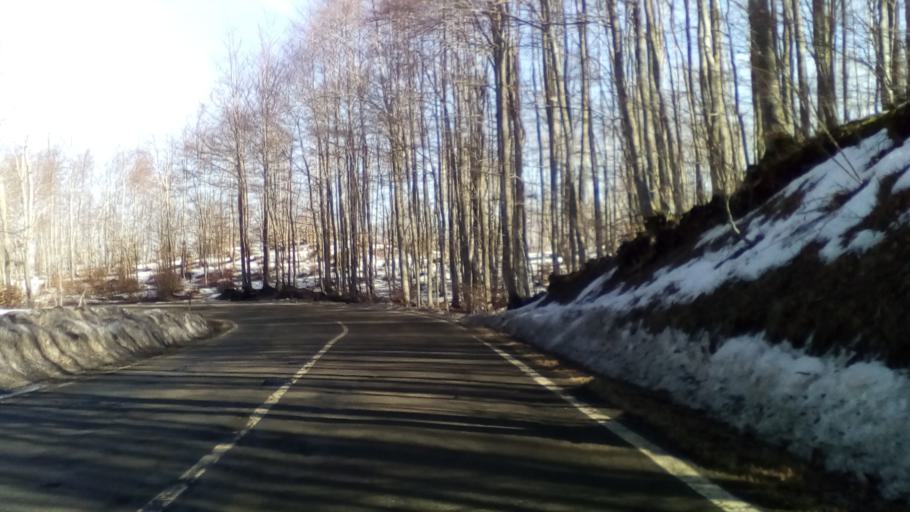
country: IT
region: Tuscany
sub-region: Provincia di Lucca
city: Fosciandora
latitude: 44.1965
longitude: 10.5129
